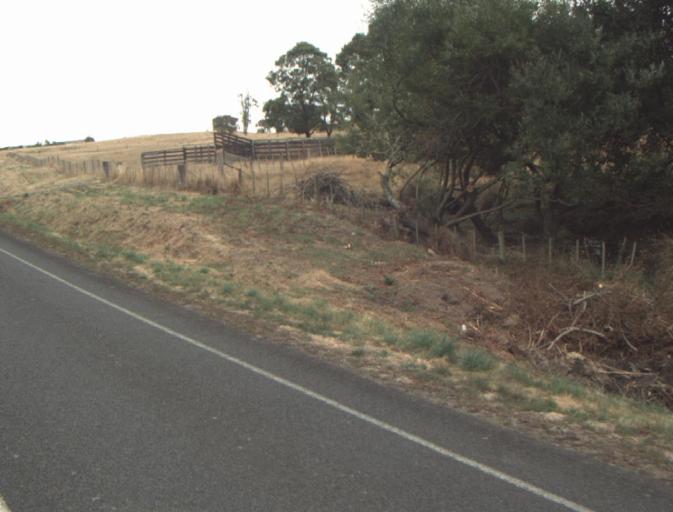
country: AU
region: Tasmania
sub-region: Launceston
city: Mayfield
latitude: -41.2803
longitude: 147.2200
